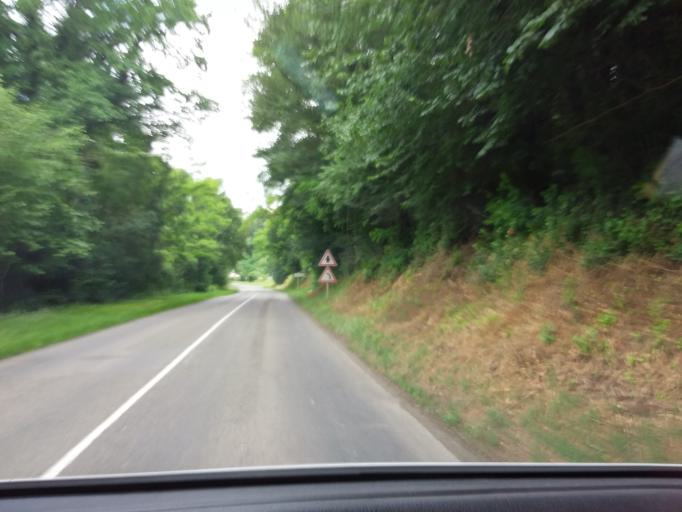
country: FR
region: Picardie
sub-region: Departement de l'Aisne
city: Vailly-sur-Aisne
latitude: 49.4095
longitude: 3.4973
